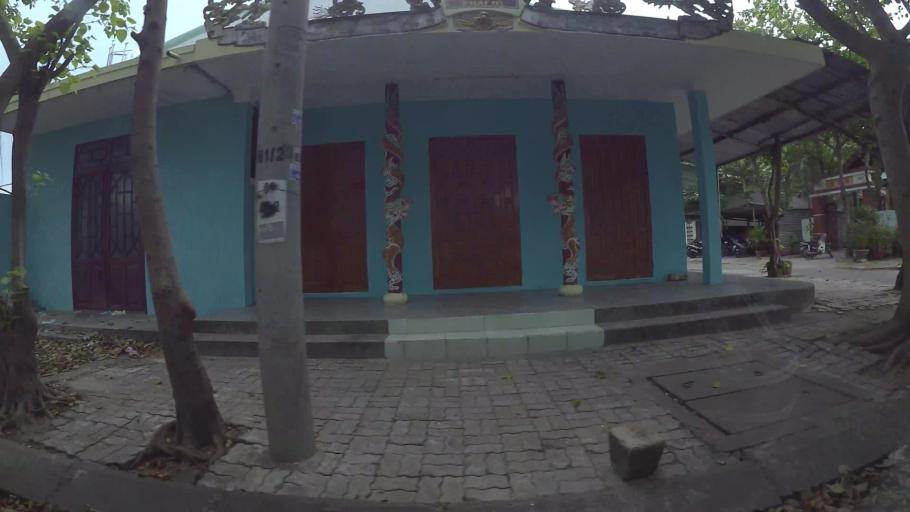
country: VN
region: Da Nang
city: Lien Chieu
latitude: 16.0739
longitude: 108.1652
